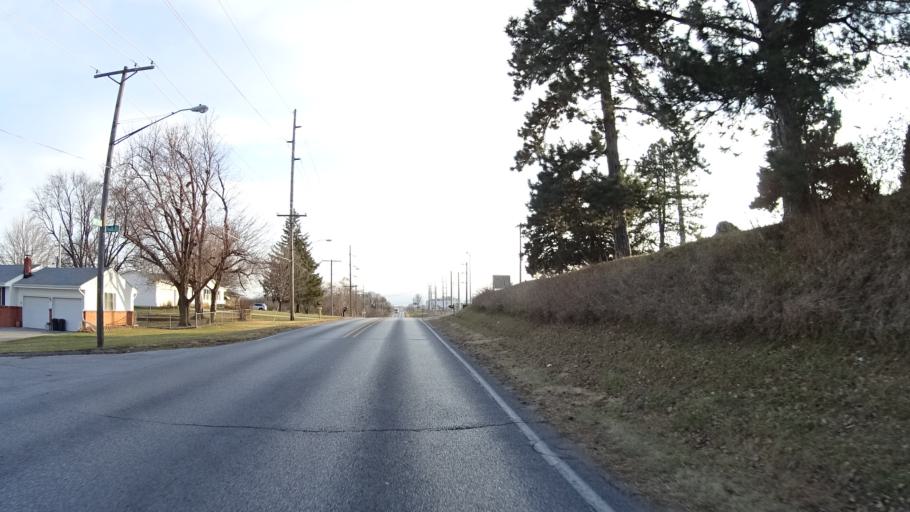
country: US
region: Nebraska
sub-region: Sarpy County
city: La Vista
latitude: 41.1716
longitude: -95.9673
